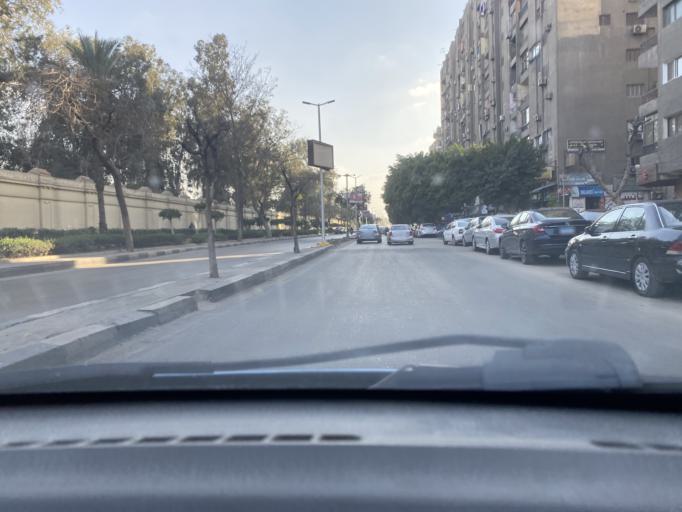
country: EG
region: Muhafazat al Qahirah
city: Cairo
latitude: 30.1010
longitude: 31.3004
